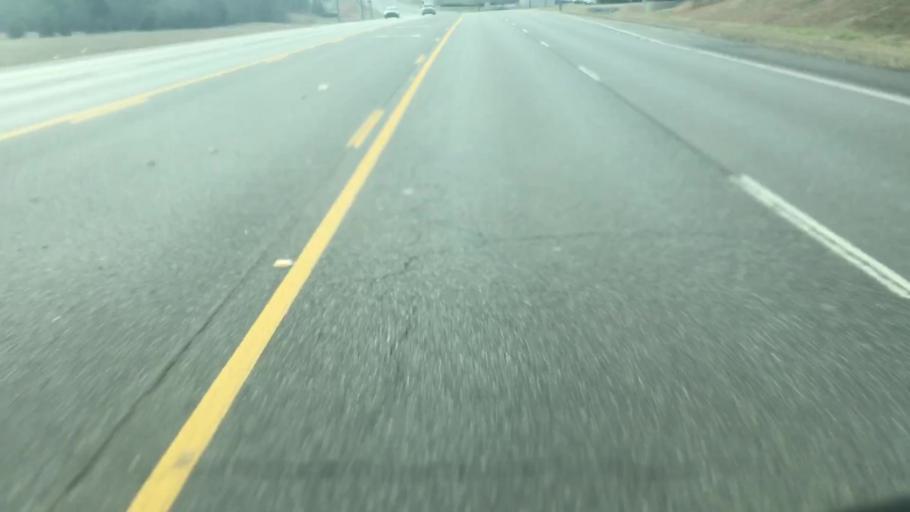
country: US
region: Alabama
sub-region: Walker County
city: Jasper
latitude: 33.8214
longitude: -87.2339
